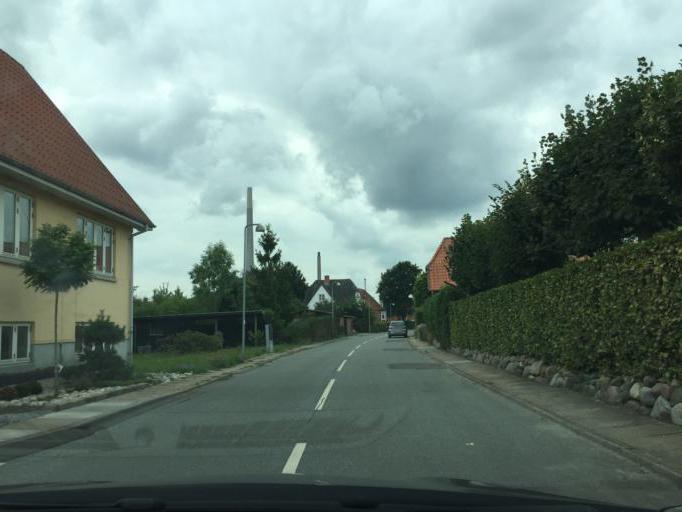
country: DK
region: South Denmark
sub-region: Odense Kommune
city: Stige
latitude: 55.4375
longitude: 10.4188
